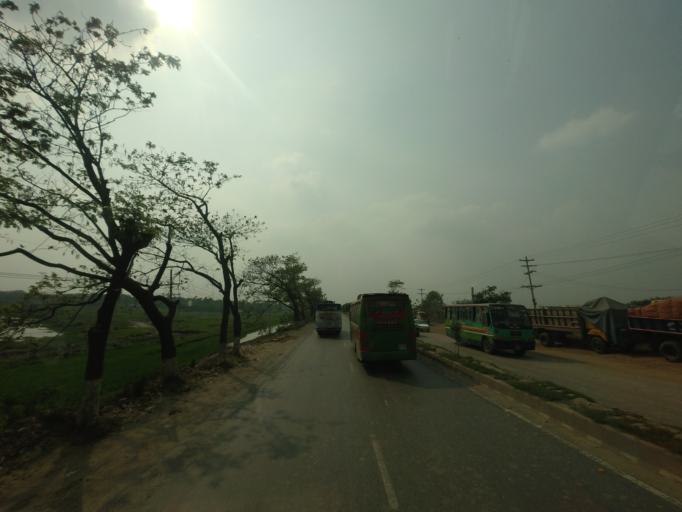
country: BD
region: Dhaka
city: Azimpur
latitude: 23.7906
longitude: 90.3103
